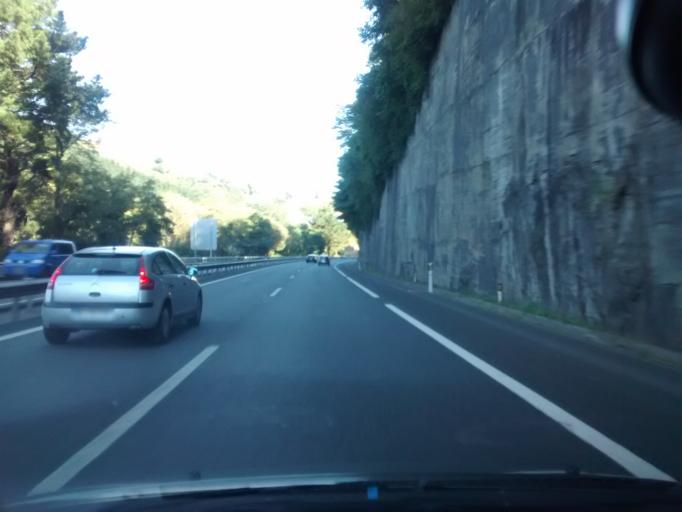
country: ES
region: Basque Country
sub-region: Provincia de Guipuzcoa
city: Deba
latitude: 43.2811
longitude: -2.3158
